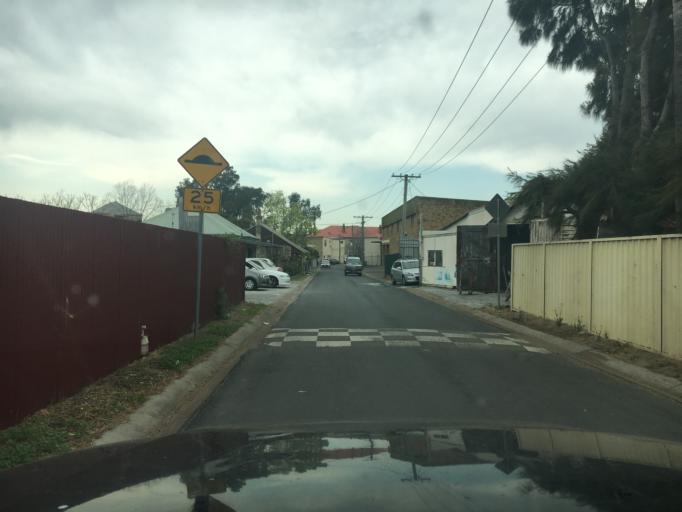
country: AU
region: New South Wales
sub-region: Maitland Municipality
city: East Maitland
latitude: -32.7468
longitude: 151.5794
